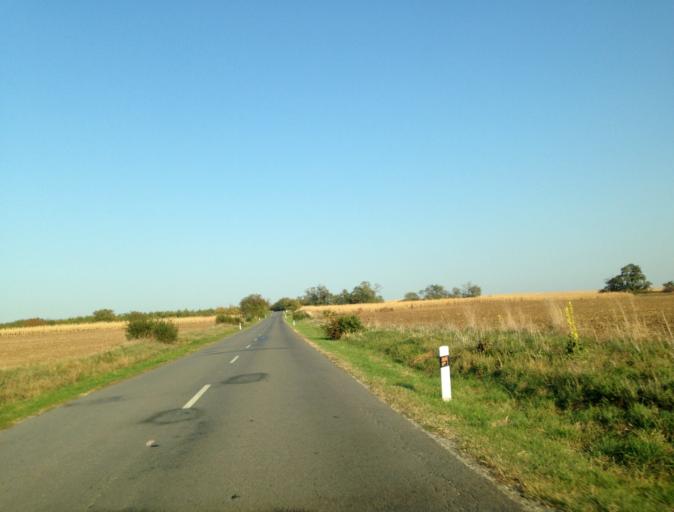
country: SK
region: Nitriansky
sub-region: Okres Komarno
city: Hurbanovo
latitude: 47.8983
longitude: 18.2688
